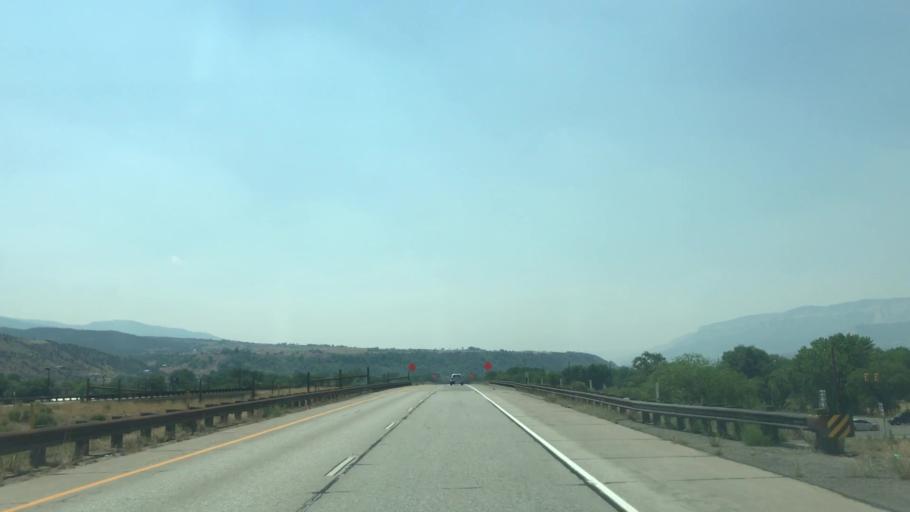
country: US
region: Colorado
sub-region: Garfield County
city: Rifle
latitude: 39.5246
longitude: -107.7763
